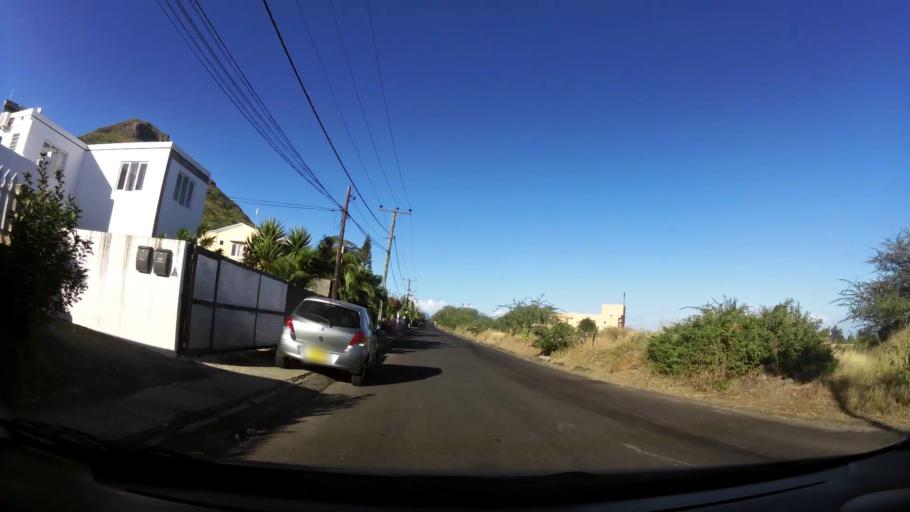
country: MU
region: Black River
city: Tamarin
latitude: -20.3353
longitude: 57.3712
